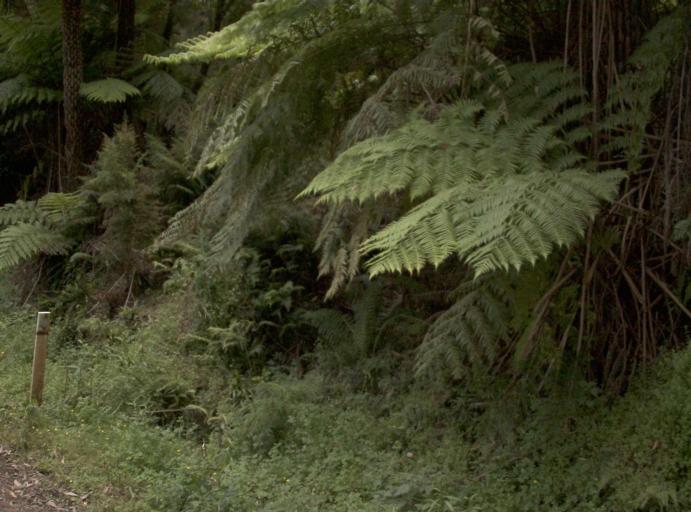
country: AU
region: Victoria
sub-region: Latrobe
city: Traralgon
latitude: -38.4664
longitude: 146.5523
